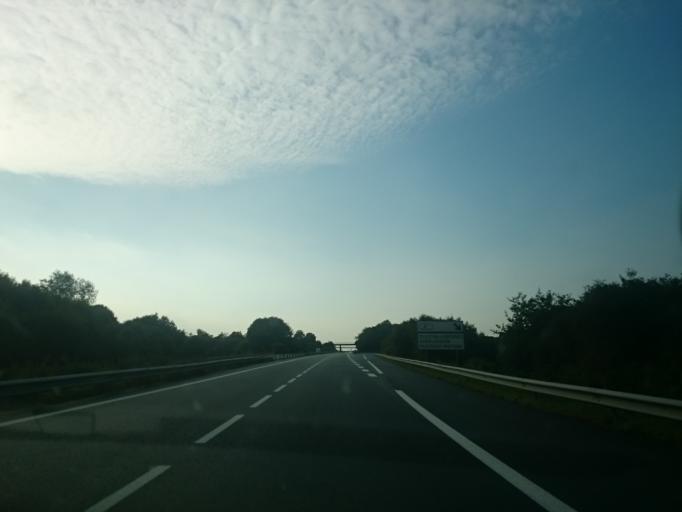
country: FR
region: Brittany
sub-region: Departement du Finistere
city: Guerlesquin
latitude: 48.5691
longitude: -3.6007
